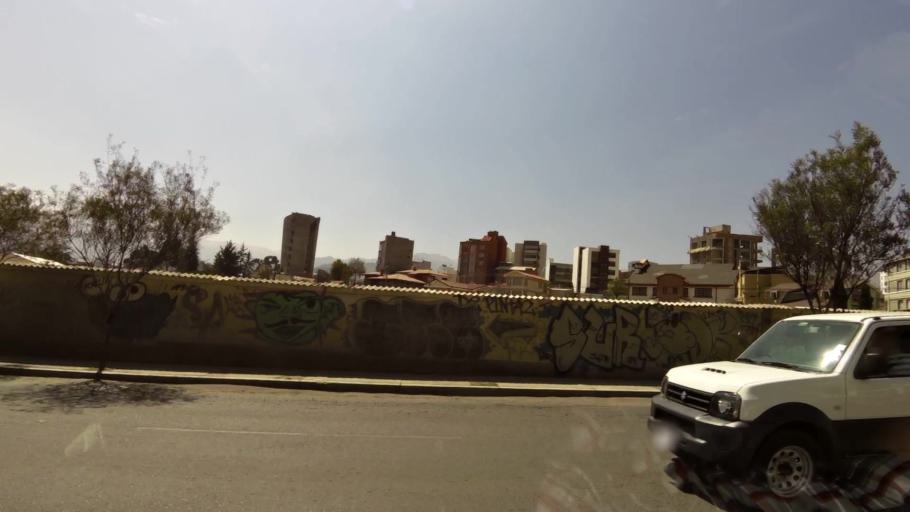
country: BO
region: La Paz
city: La Paz
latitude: -16.5458
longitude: -68.0814
